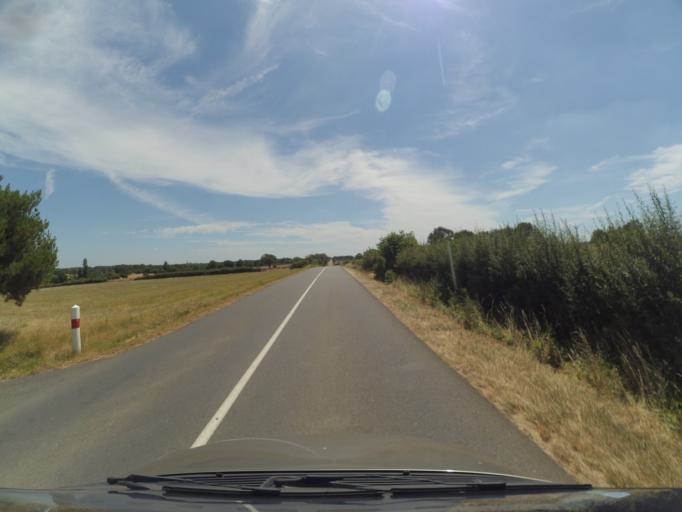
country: FR
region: Poitou-Charentes
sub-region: Departement de la Vienne
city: Usson-du-Poitou
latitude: 46.2451
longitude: 0.5247
